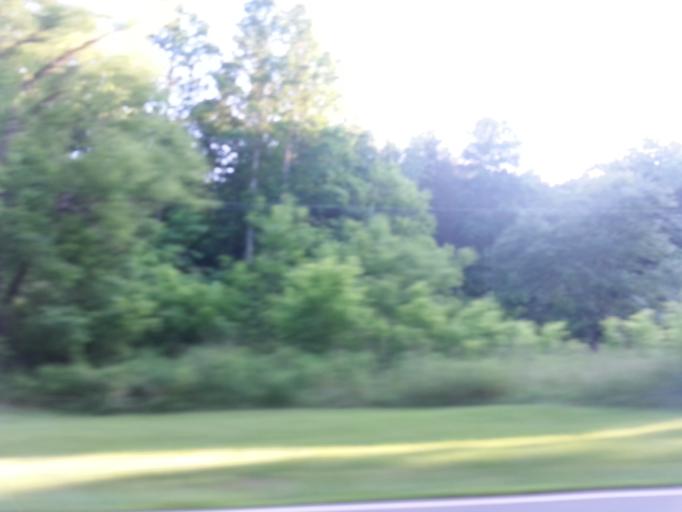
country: US
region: North Carolina
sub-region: Cherokee County
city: Murphy
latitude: 35.0426
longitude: -84.1466
